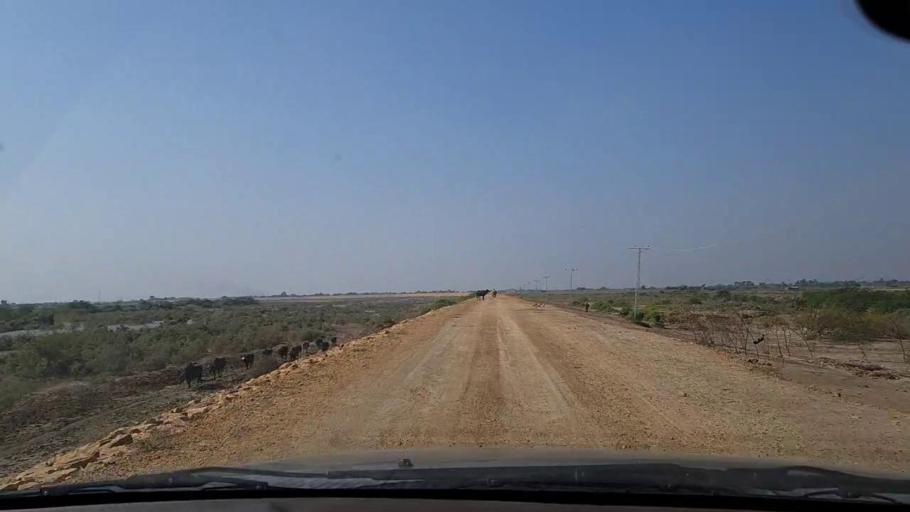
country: PK
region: Sindh
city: Chuhar Jamali
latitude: 24.4556
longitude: 67.8748
